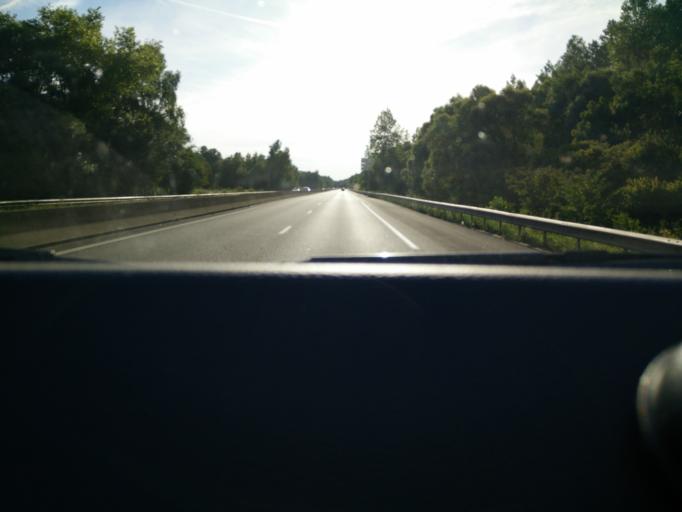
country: FR
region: Nord-Pas-de-Calais
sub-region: Departement du Nord
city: Pecquencourt
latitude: 50.3827
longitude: 3.2040
